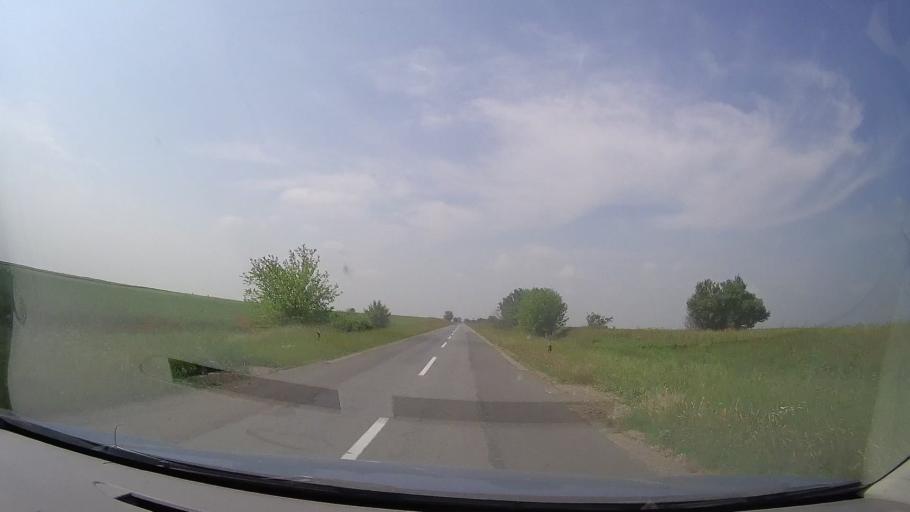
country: RS
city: Padina
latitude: 45.1549
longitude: 20.7470
